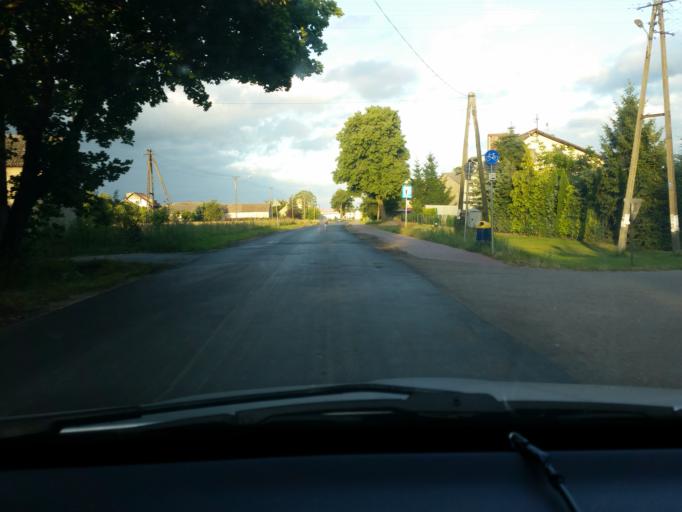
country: PL
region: Pomeranian Voivodeship
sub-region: Powiat czluchowski
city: Przechlewo
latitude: 53.8210
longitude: 17.3910
